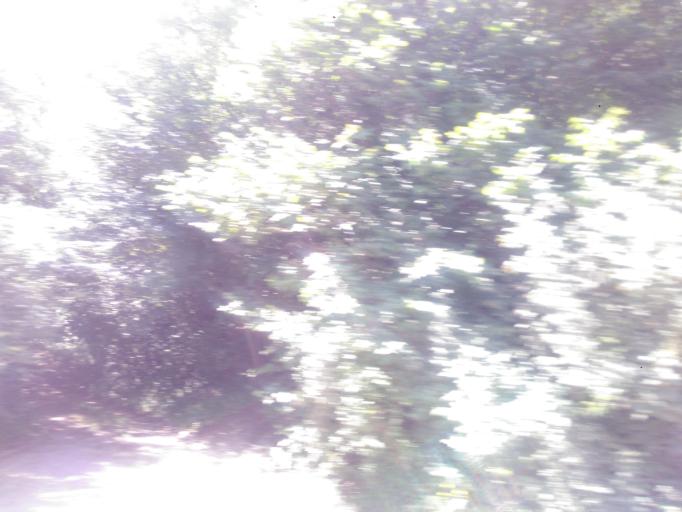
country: GE
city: Zhinvali
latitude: 42.1804
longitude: 44.8168
